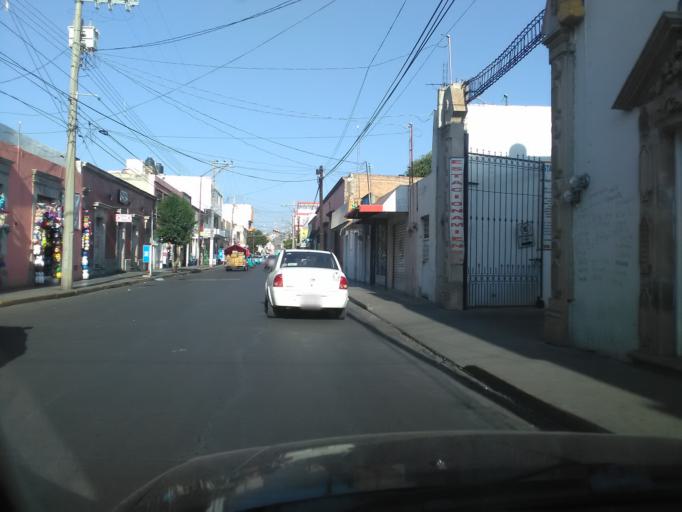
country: MX
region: Durango
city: Victoria de Durango
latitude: 24.0245
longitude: -104.6631
